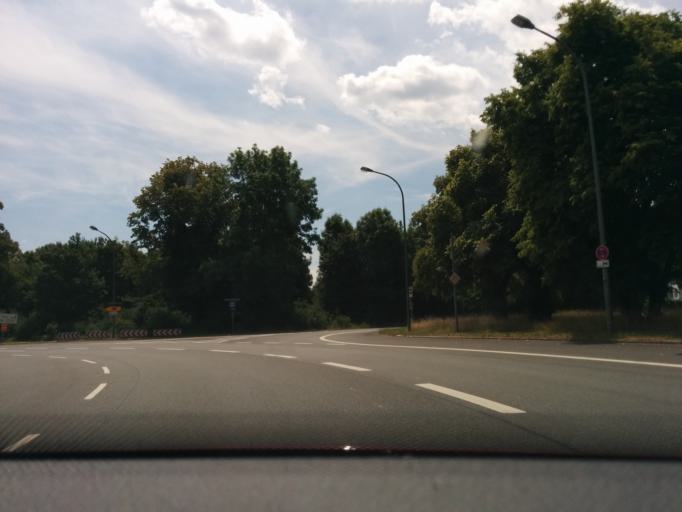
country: DE
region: Bavaria
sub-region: Upper Bavaria
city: Pasing
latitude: 48.1664
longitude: 11.4540
